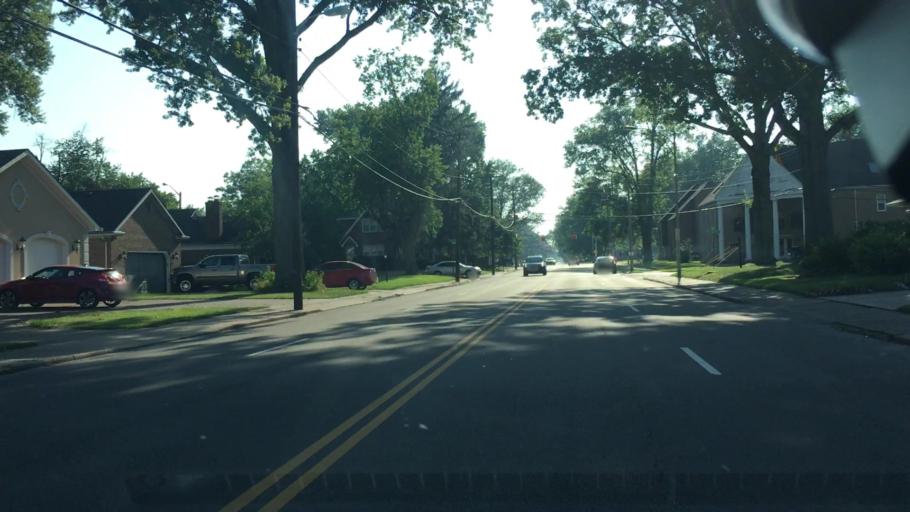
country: US
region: Indiana
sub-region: Vanderburgh County
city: Evansville
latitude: 37.9736
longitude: -87.5275
